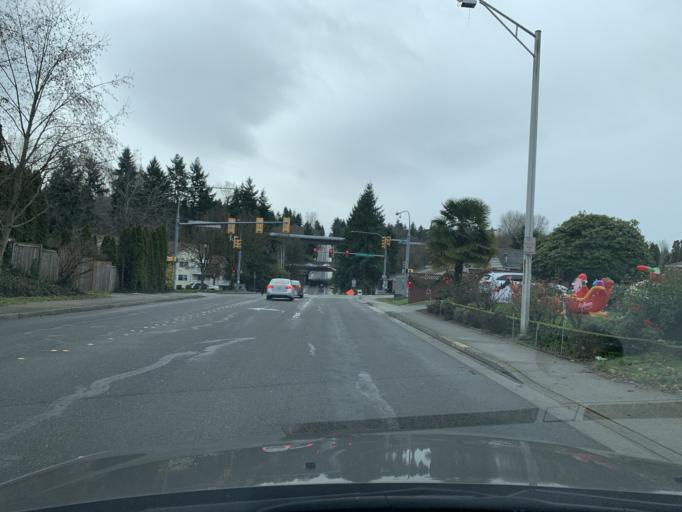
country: US
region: Washington
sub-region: King County
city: SeaTac
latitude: 47.4665
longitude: -122.2812
